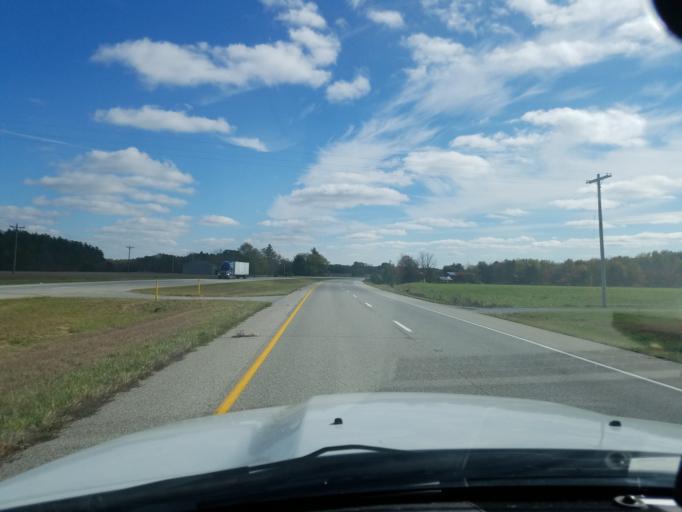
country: US
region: Indiana
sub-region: Dearborn County
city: Dillsboro
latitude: 39.0472
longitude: -85.1108
